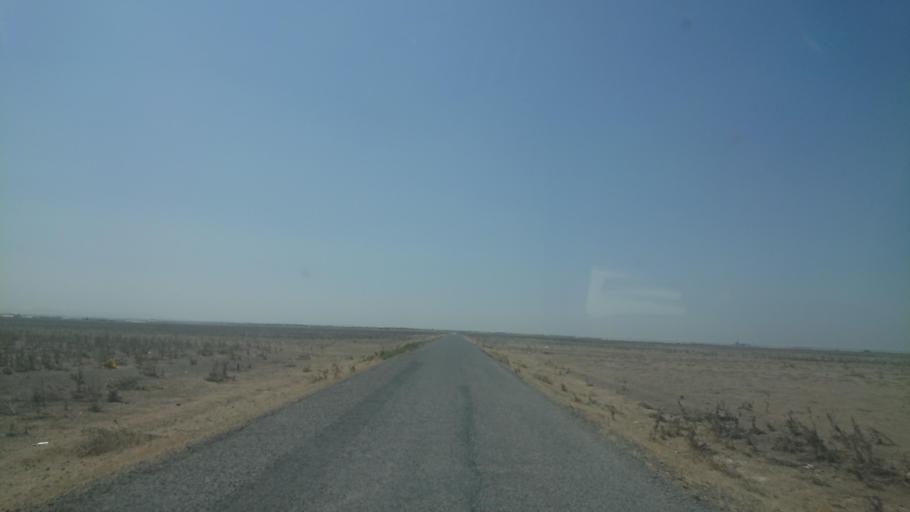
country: TR
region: Aksaray
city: Yesilova
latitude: 38.3240
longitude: 33.7454
